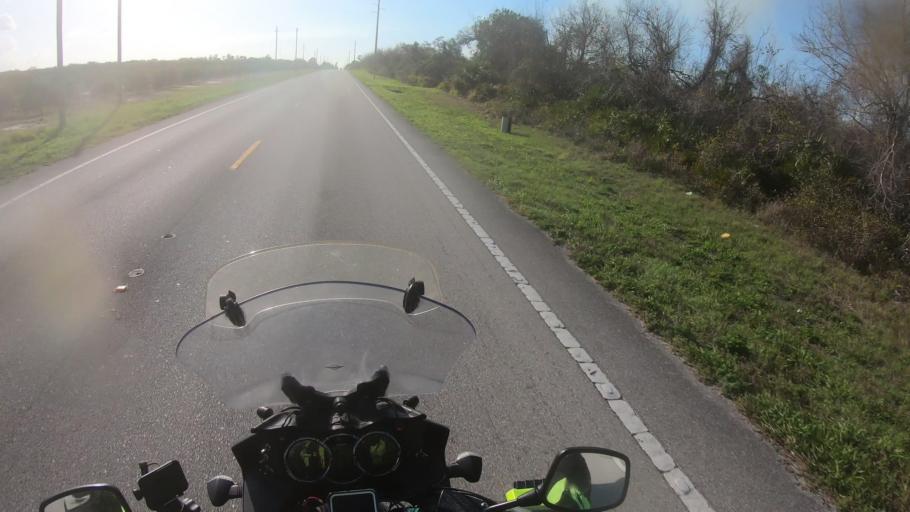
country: US
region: Florida
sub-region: Highlands County
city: Placid Lakes
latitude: 27.2088
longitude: -81.3726
